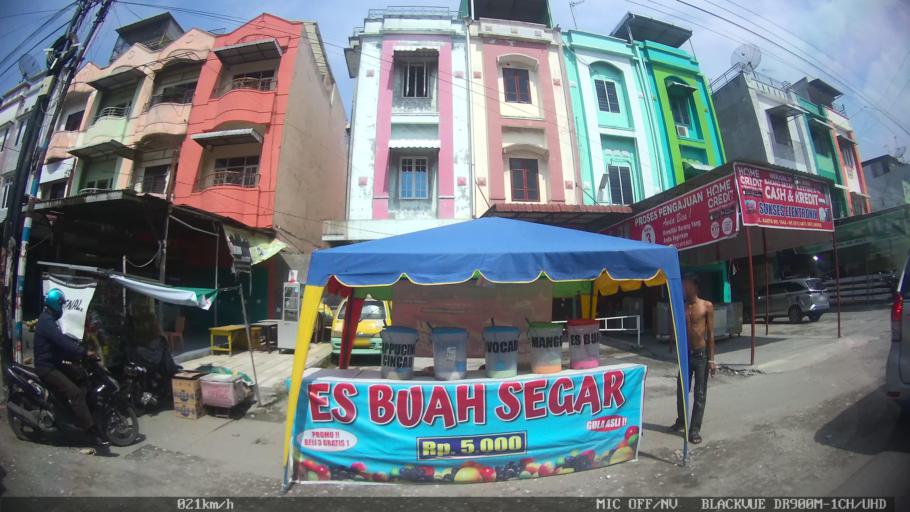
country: ID
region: North Sumatra
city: Medan
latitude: 3.6128
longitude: 98.6656
